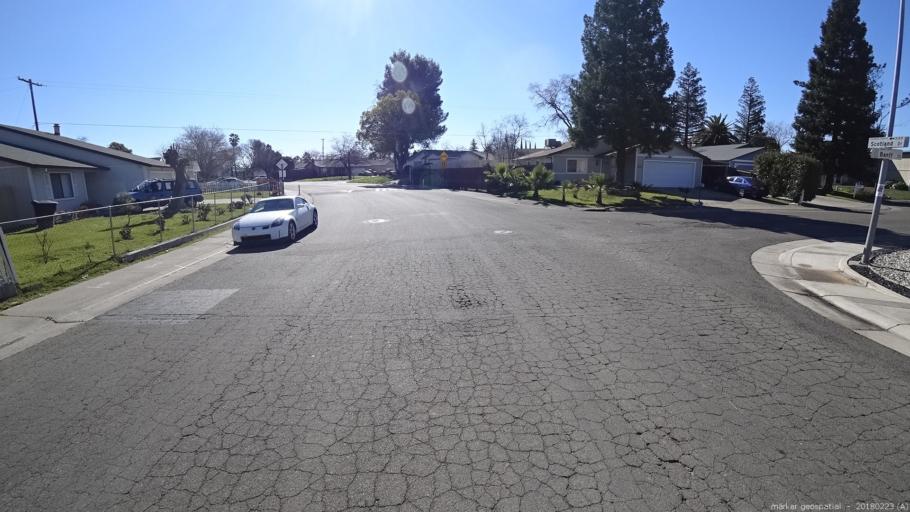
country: US
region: California
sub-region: Sacramento County
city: North Highlands
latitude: 38.7078
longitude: -121.3945
